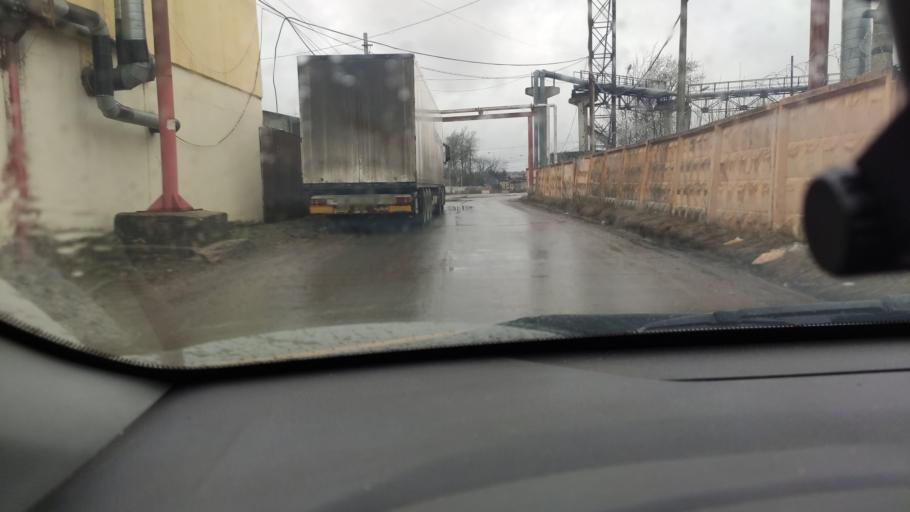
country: RU
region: Moskovskaya
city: Selyatino
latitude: 55.5135
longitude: 36.9650
